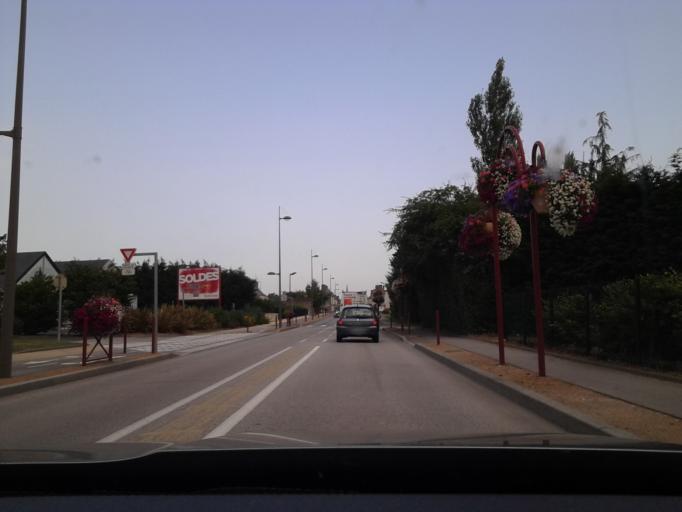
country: FR
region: Lower Normandy
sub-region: Departement de la Manche
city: Valognes
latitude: 49.5124
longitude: -1.4795
